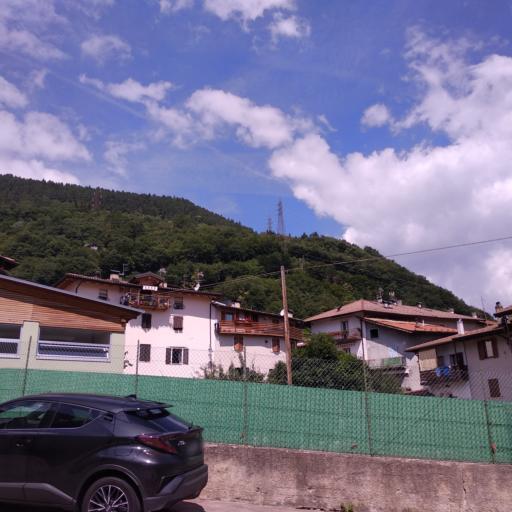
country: IT
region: Trentino-Alto Adige
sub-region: Provincia di Trento
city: Trento
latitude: 46.0636
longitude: 11.0968
